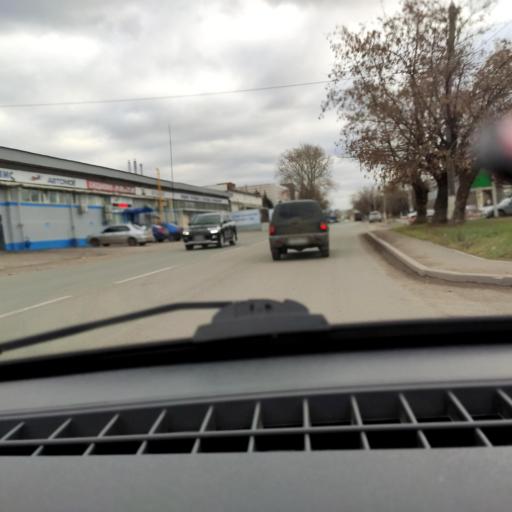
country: RU
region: Bashkortostan
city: Ufa
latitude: 54.8080
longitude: 56.0787
